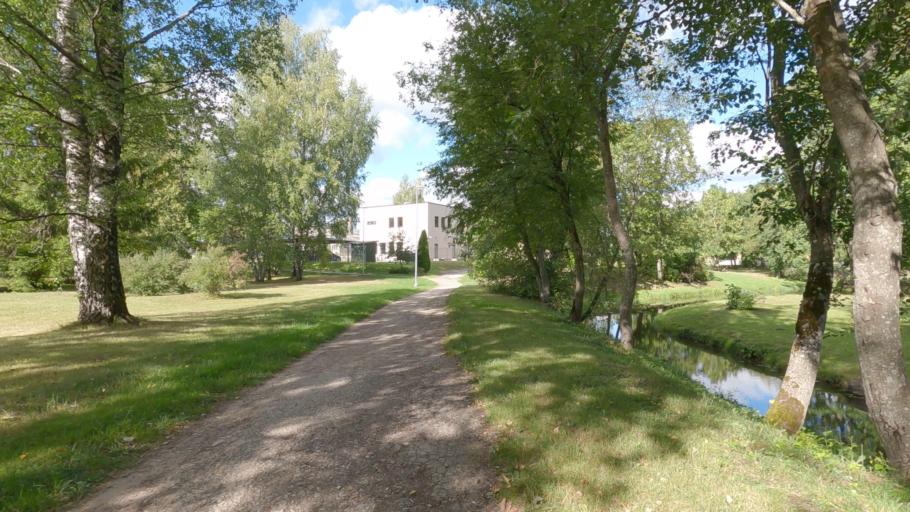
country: EE
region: Raplamaa
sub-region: Rapla vald
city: Rapla
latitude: 59.0066
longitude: 24.7892
